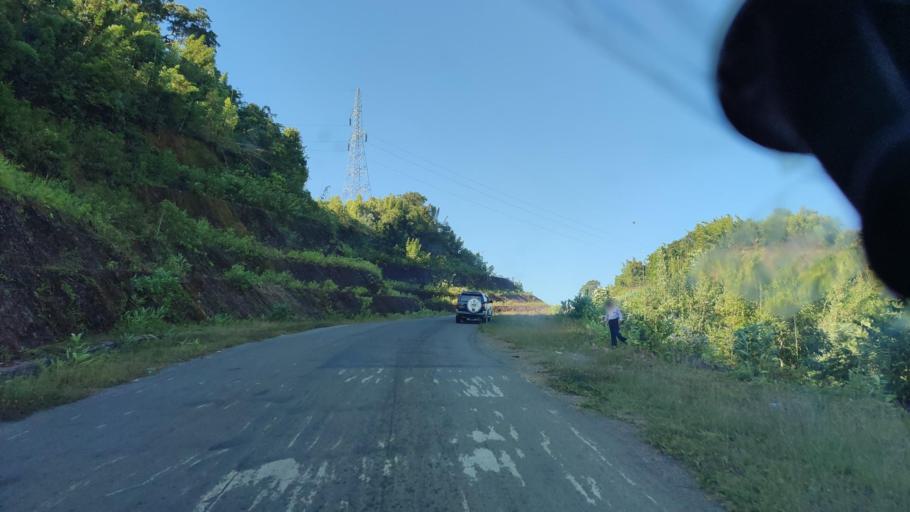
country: MM
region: Rakhine
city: Sittwe
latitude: 19.9305
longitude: 93.7695
